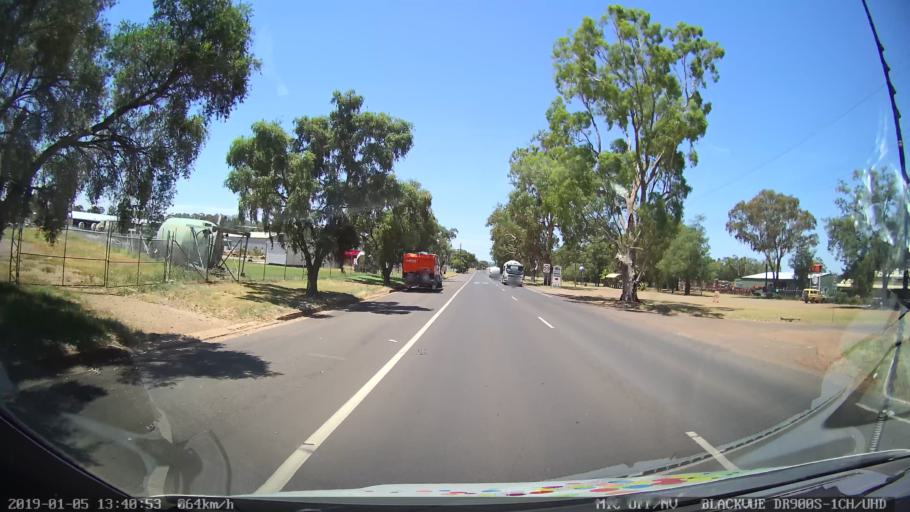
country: AU
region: New South Wales
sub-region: Gunnedah
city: Gunnedah
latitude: -30.9802
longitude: 150.2344
